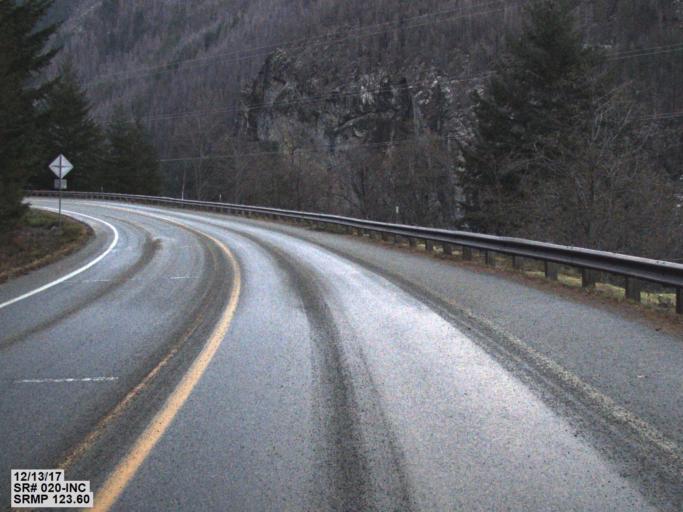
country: US
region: Washington
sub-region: Snohomish County
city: Darrington
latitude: 48.7006
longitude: -121.2071
